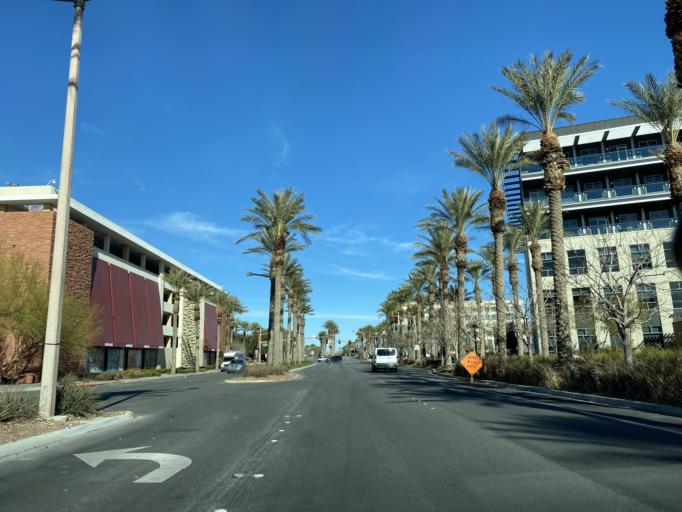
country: US
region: Nevada
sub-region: Clark County
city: Summerlin South
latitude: 36.1556
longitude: -115.3306
